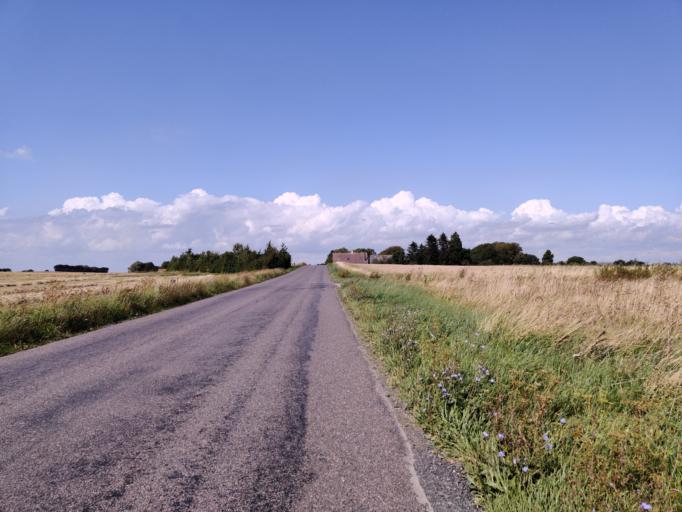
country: DK
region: Zealand
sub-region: Guldborgsund Kommune
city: Nykobing Falster
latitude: 54.6160
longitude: 11.9166
